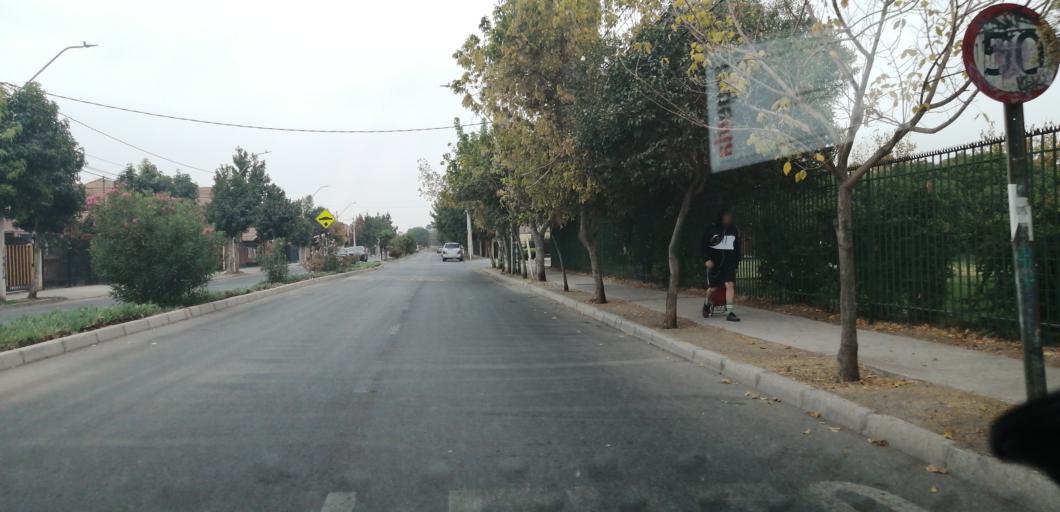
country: CL
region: Santiago Metropolitan
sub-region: Provincia de Santiago
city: Lo Prado
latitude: -33.4521
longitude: -70.7632
